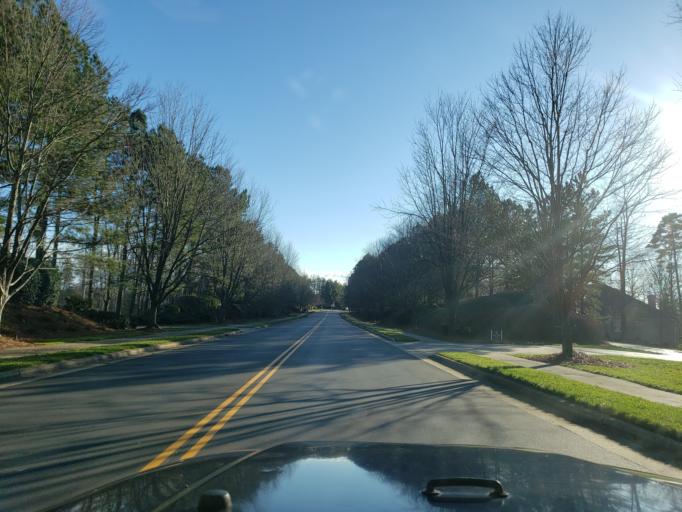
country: US
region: North Carolina
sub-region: Lincoln County
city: Westport
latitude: 35.5311
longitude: -80.9229
